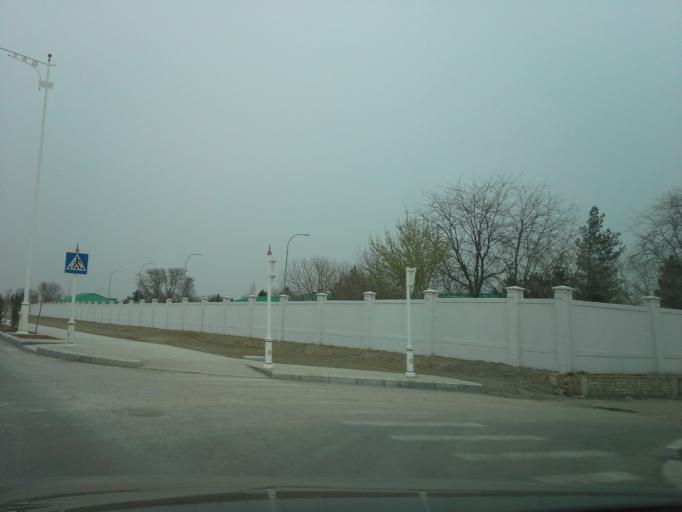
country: TM
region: Ahal
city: Ashgabat
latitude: 37.9595
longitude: 58.3398
